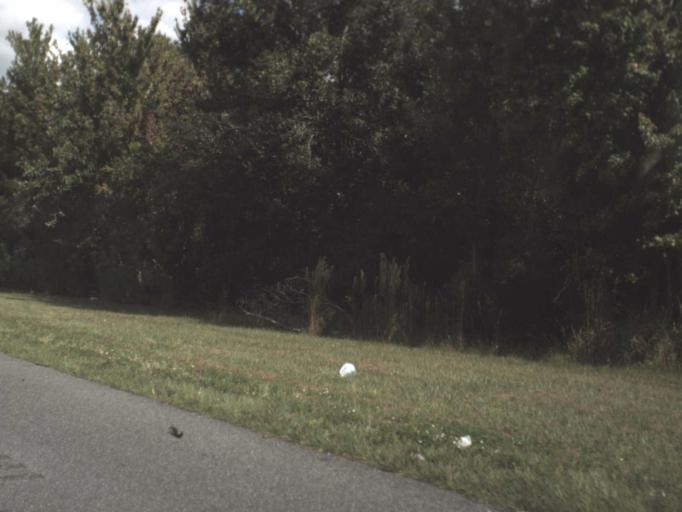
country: US
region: Florida
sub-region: Orange County
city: Southchase
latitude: 28.3831
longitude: -81.3910
